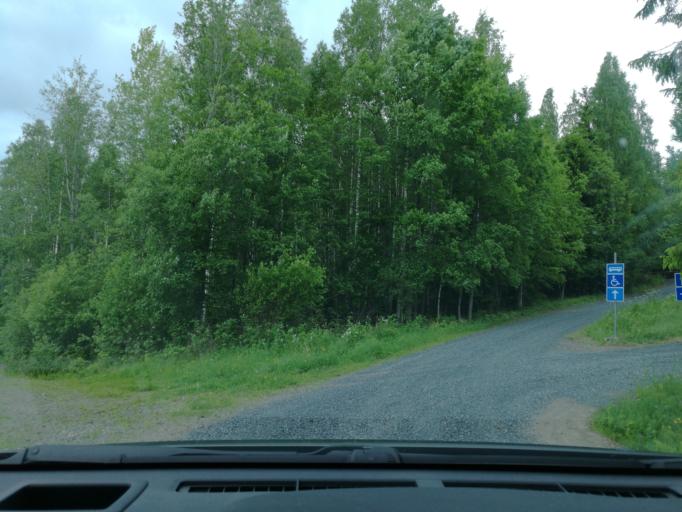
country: SE
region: Dalarna
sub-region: Smedjebackens Kommun
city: Smedjebacken
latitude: 60.1458
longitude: 15.3035
